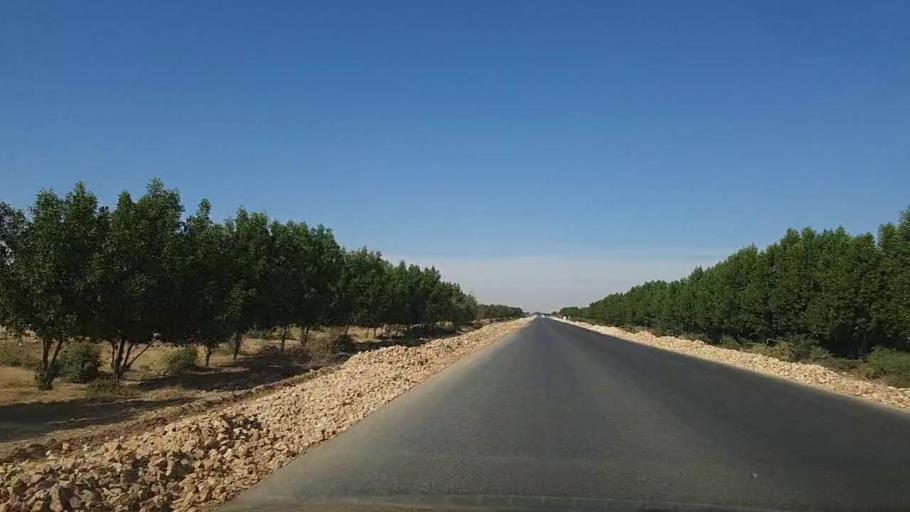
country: PK
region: Sindh
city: Kotri
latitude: 25.2708
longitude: 68.2172
